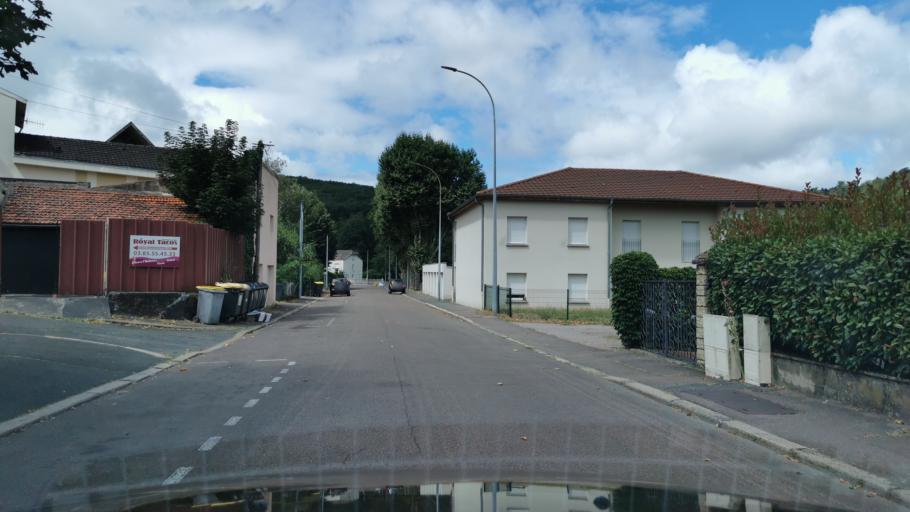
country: FR
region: Bourgogne
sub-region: Departement de Saone-et-Loire
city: Le Creusot
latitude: 46.8061
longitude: 4.4164
